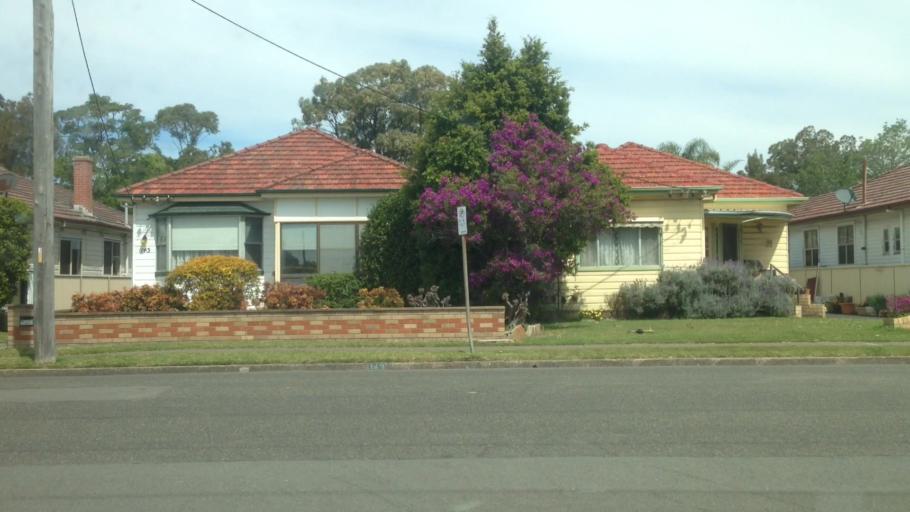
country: AU
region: New South Wales
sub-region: Newcastle
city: Broadmeadow
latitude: -32.9325
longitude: 151.7367
